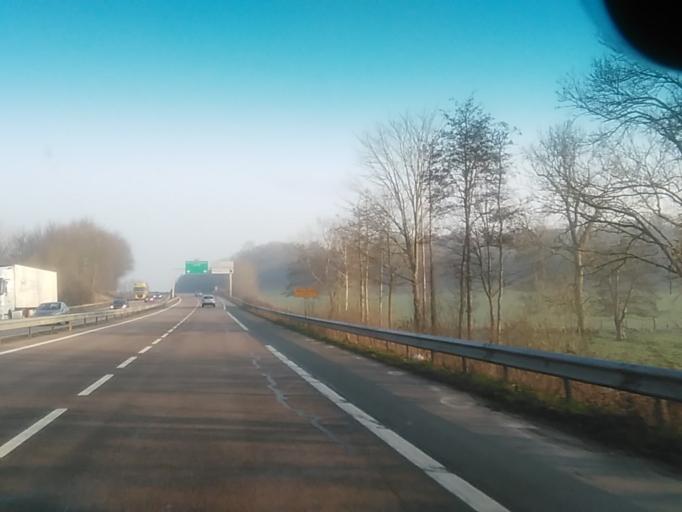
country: FR
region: Lower Normandy
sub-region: Departement du Calvados
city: Potigny
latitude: 48.9706
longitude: -0.2369
